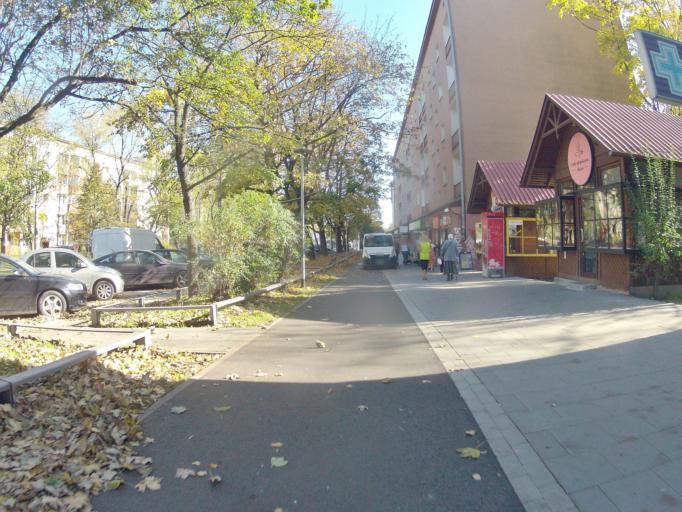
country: PL
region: Lesser Poland Voivodeship
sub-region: Krakow
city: Krakow
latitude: 50.0735
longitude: 19.9128
